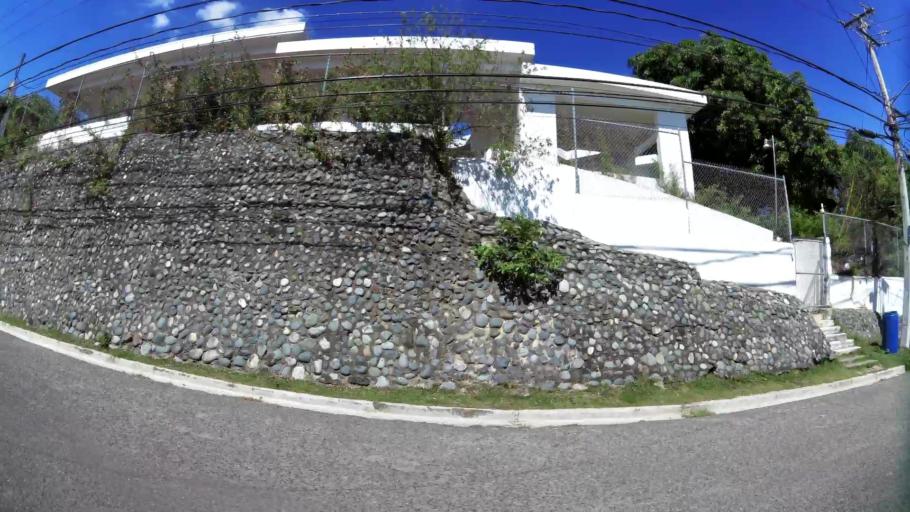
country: DO
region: Santiago
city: Santiago de los Caballeros
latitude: 19.4457
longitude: -70.6921
